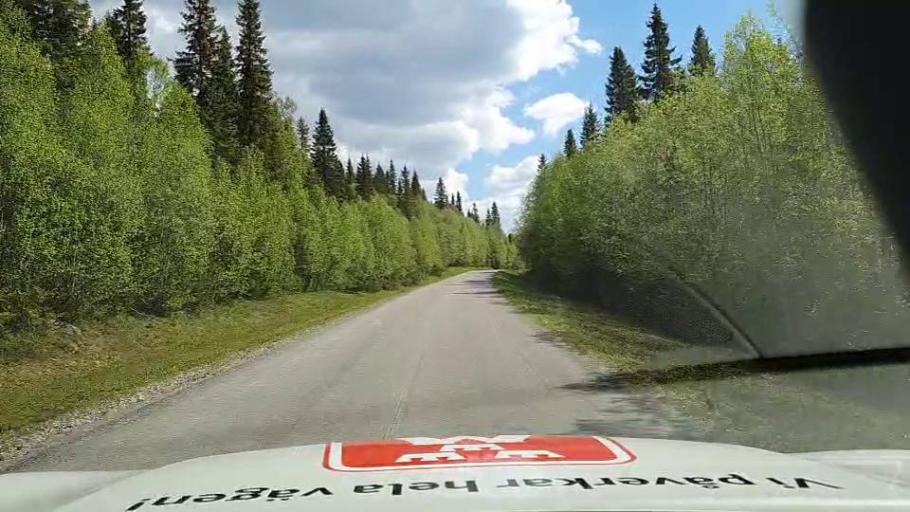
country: NO
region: Nord-Trondelag
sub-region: Lierne
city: Sandvika
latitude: 64.1321
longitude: 14.1173
